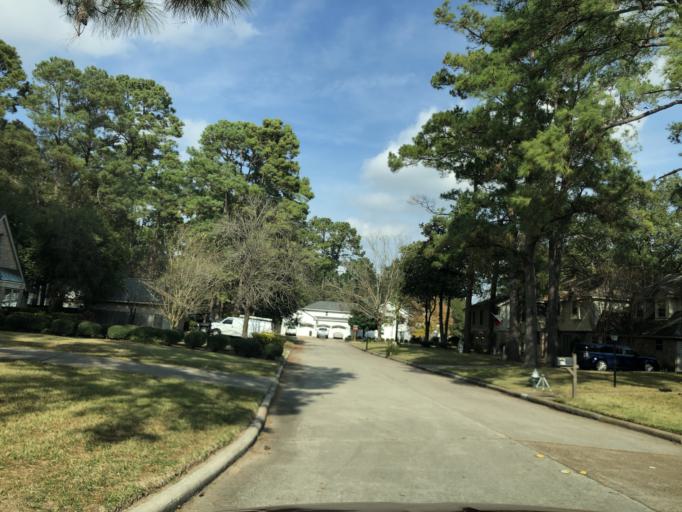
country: US
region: Texas
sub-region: Harris County
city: Tomball
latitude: 30.0241
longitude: -95.5475
